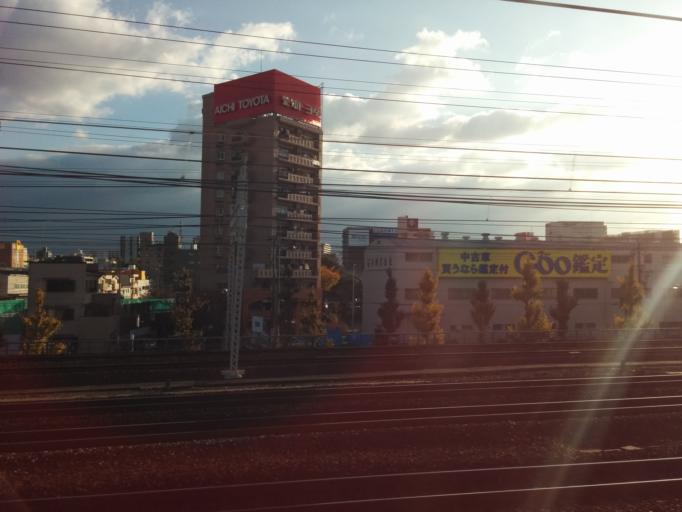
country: JP
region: Aichi
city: Nagoya-shi
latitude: 35.1552
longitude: 136.8874
